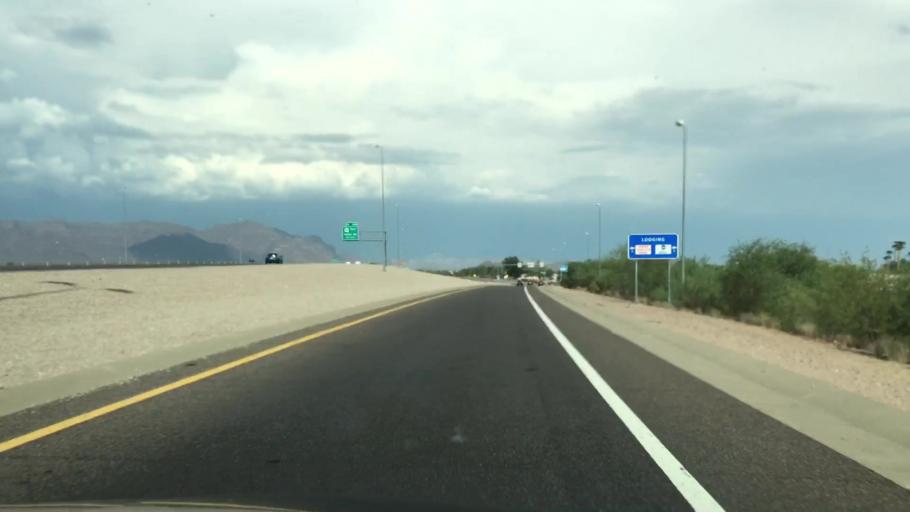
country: US
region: Arizona
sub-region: Pinal County
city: Apache Junction
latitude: 33.3864
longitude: -111.5670
